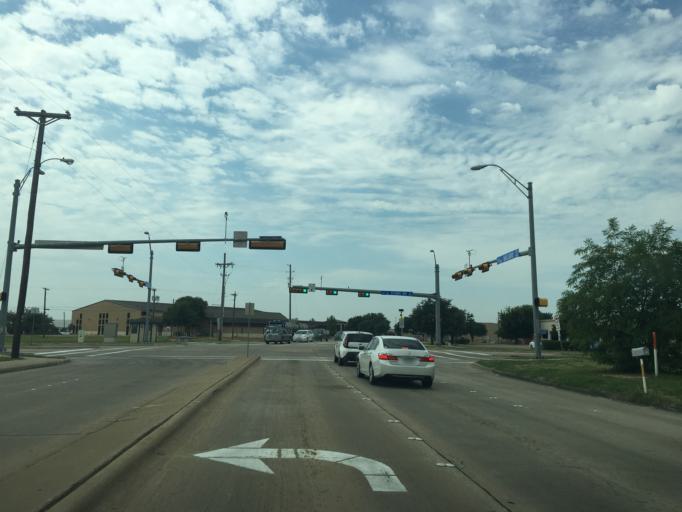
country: US
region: Texas
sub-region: Collin County
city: Wylie
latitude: 33.0067
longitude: -96.5391
